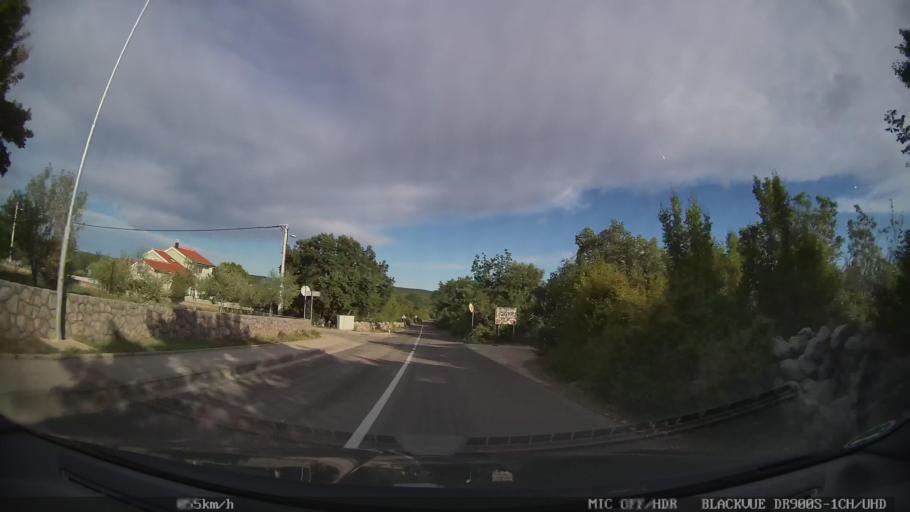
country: HR
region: Primorsko-Goranska
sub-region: Grad Krk
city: Krk
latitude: 45.0601
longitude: 14.4810
